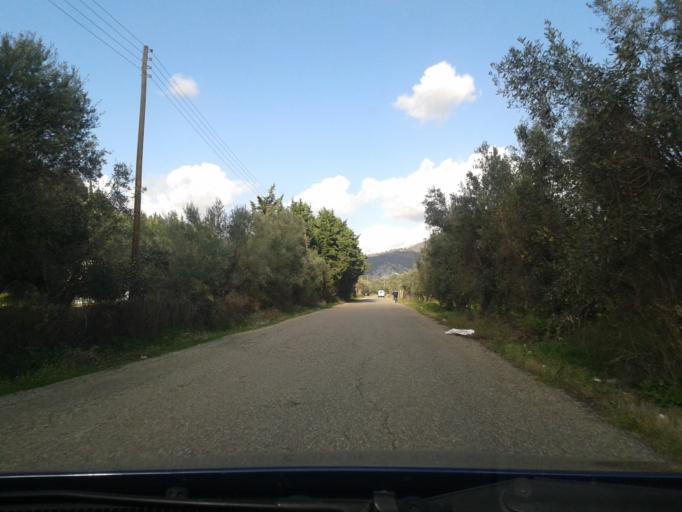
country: GR
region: West Greece
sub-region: Nomos Aitolias kai Akarnanias
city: Astakos
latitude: 38.5509
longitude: 21.0945
